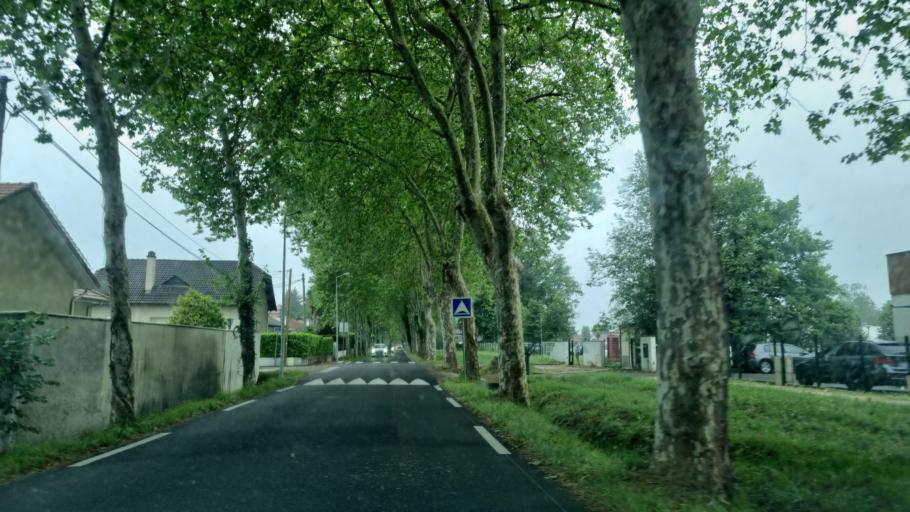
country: FR
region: Aquitaine
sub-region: Departement des Pyrenees-Atlantiques
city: Buros
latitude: 43.3251
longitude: -0.3301
